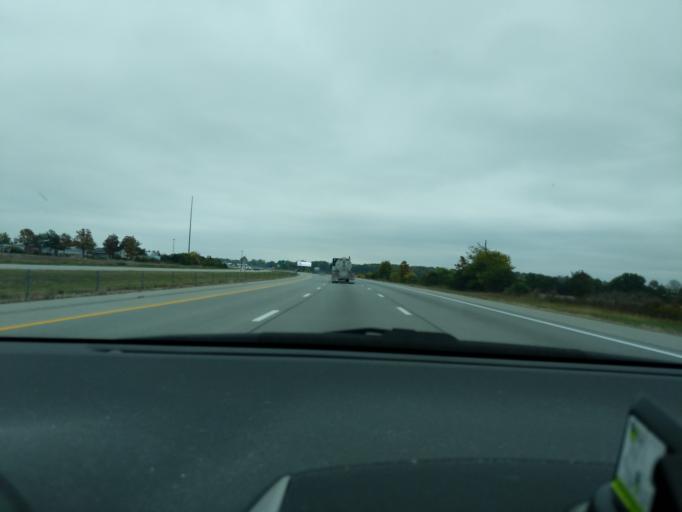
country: US
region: Ohio
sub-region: Clark County
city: Springfield
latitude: 39.8915
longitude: -83.7377
